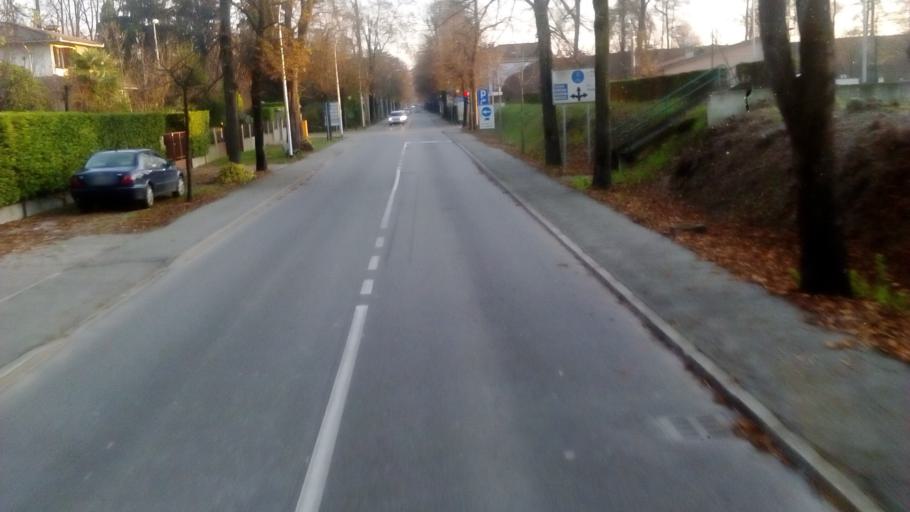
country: IT
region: Lombardy
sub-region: Provincia di Cremona
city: Castelleone
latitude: 45.3012
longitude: 9.7574
